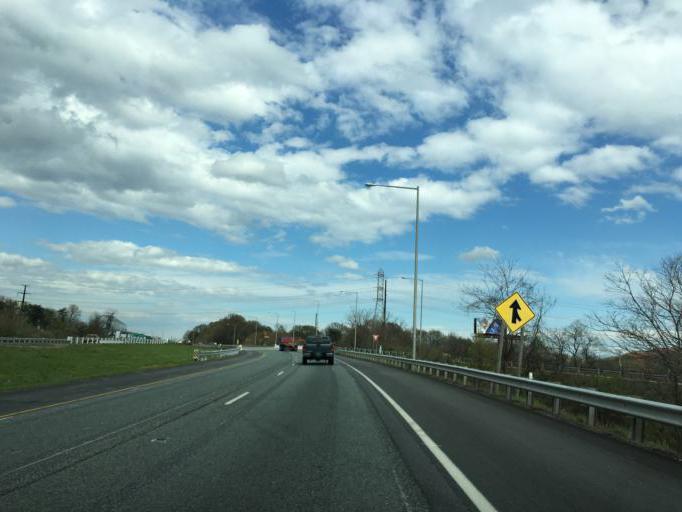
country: US
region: Maryland
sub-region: Baltimore County
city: Dundalk
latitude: 39.2038
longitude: -76.5512
